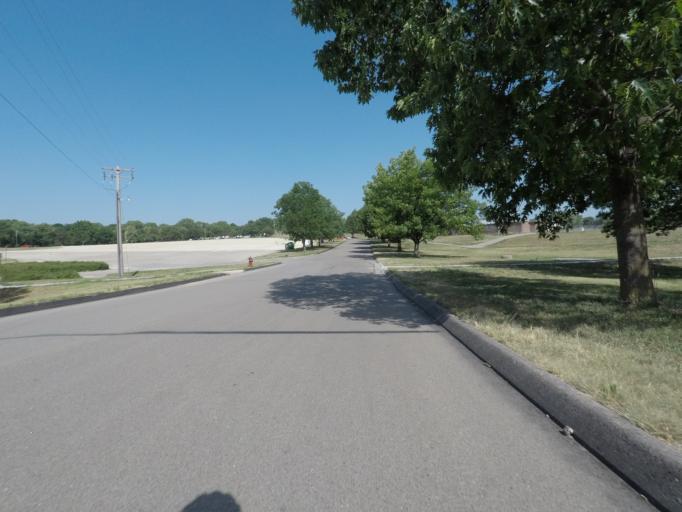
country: US
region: Kansas
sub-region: Riley County
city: Manhattan
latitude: 39.1984
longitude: -96.6183
